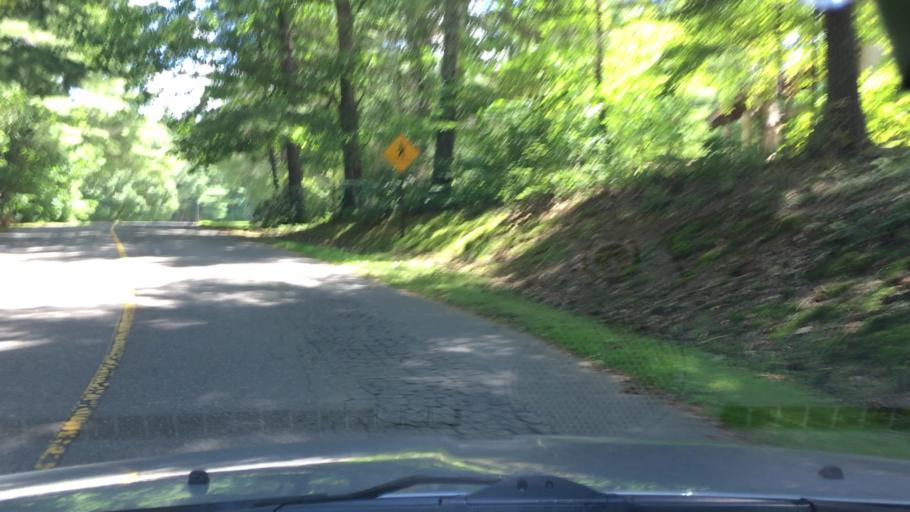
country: US
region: North Carolina
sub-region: Buncombe County
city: Asheville
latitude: 35.5931
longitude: -82.4819
